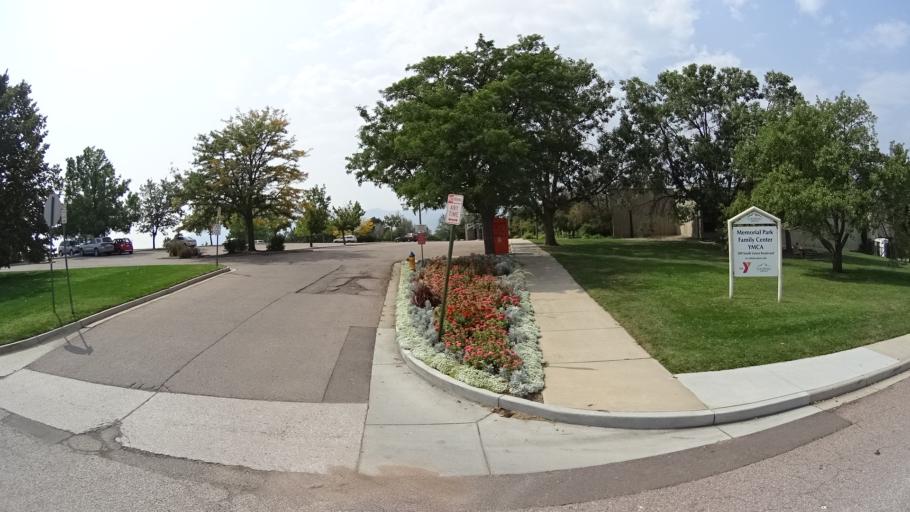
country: US
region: Colorado
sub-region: El Paso County
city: Colorado Springs
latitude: 38.8281
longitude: -104.7966
